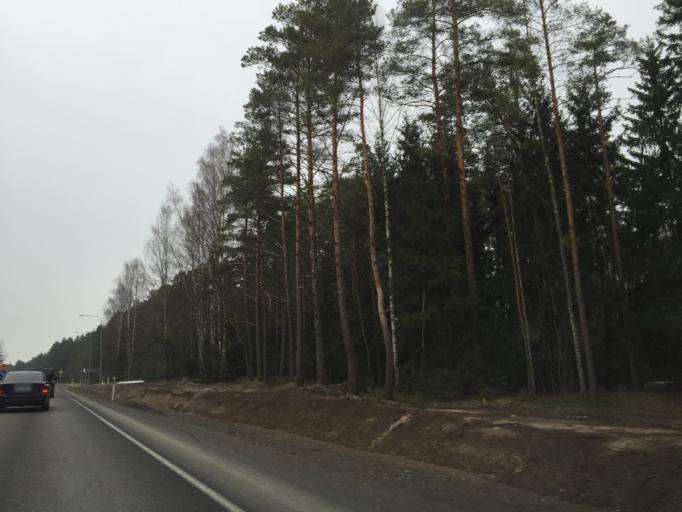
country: EE
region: Paernumaa
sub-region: Paikuse vald
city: Paikuse
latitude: 58.3245
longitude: 24.5977
